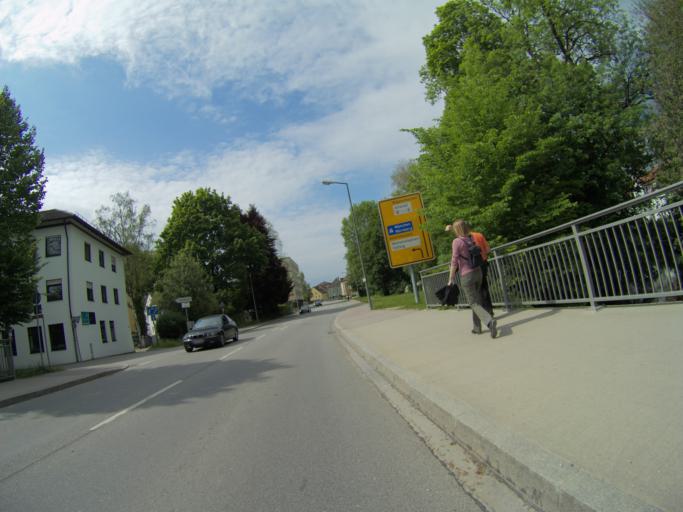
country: DE
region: Bavaria
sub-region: Upper Bavaria
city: Freising
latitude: 48.3971
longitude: 11.7398
